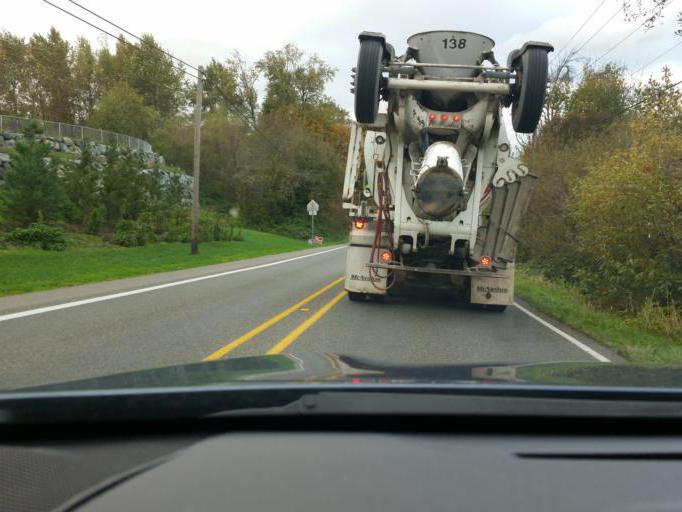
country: US
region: Washington
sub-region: Snohomish County
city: Cathcart
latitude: 47.8676
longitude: -122.0992
